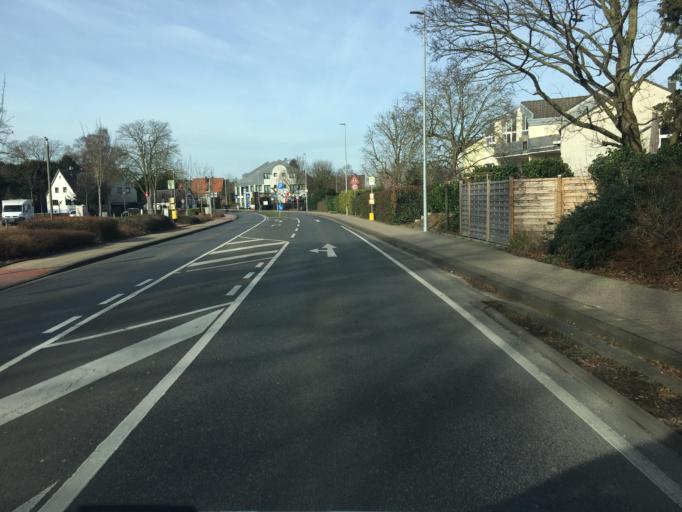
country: DE
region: North Rhine-Westphalia
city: Erkelenz
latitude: 51.0819
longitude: 6.3173
